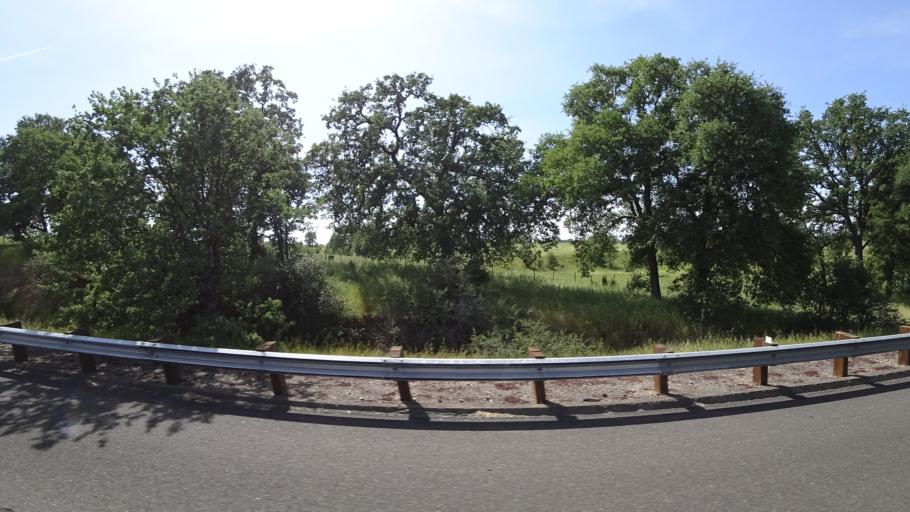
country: US
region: California
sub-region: Shasta County
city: Cottonwood
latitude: 40.3483
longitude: -122.2829
